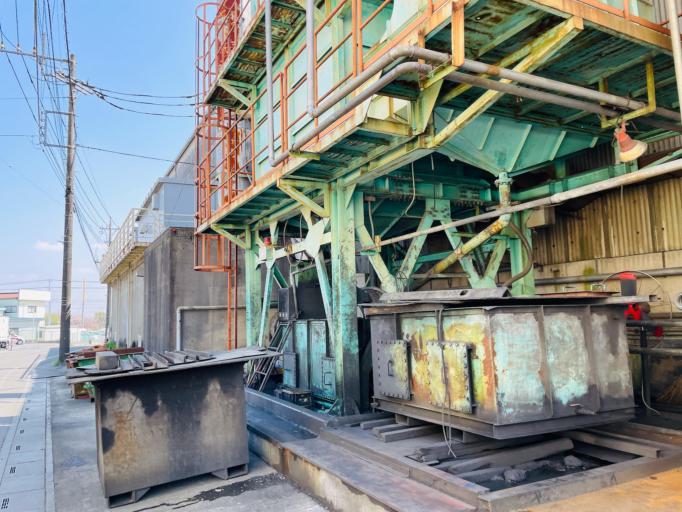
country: JP
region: Saitama
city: Sayama
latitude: 35.8733
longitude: 139.3970
